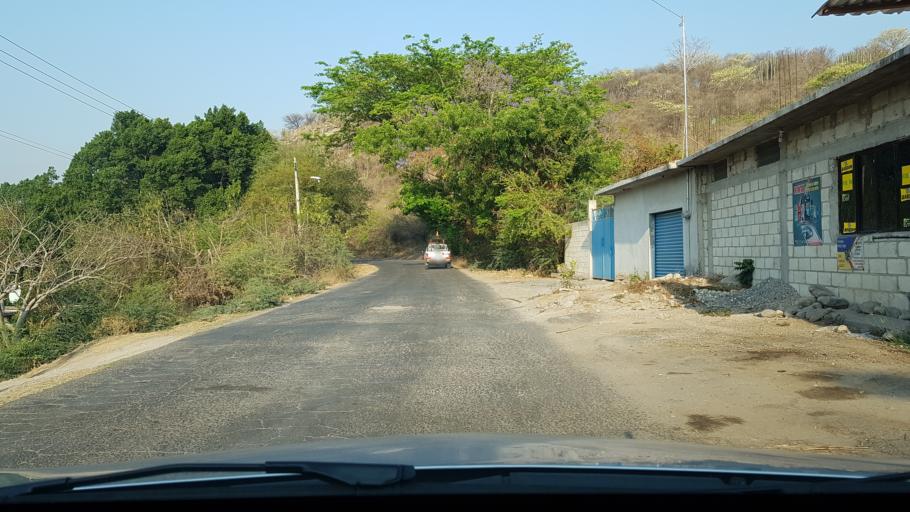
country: MX
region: Morelos
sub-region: Tepalcingo
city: Zacapalco
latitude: 18.6381
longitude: -99.0092
